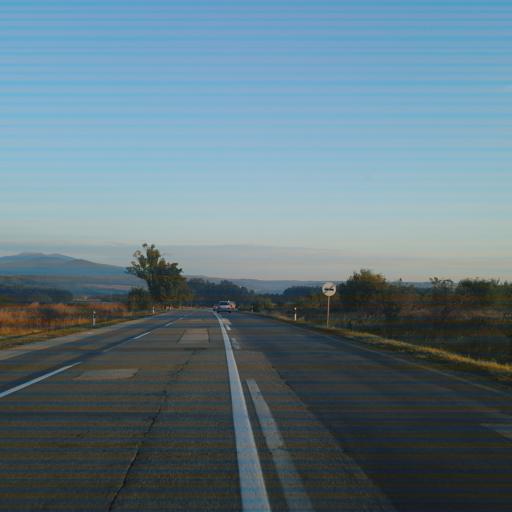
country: RS
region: Central Serbia
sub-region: Zajecarski Okrug
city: Zajecar
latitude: 44.0694
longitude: 22.3344
